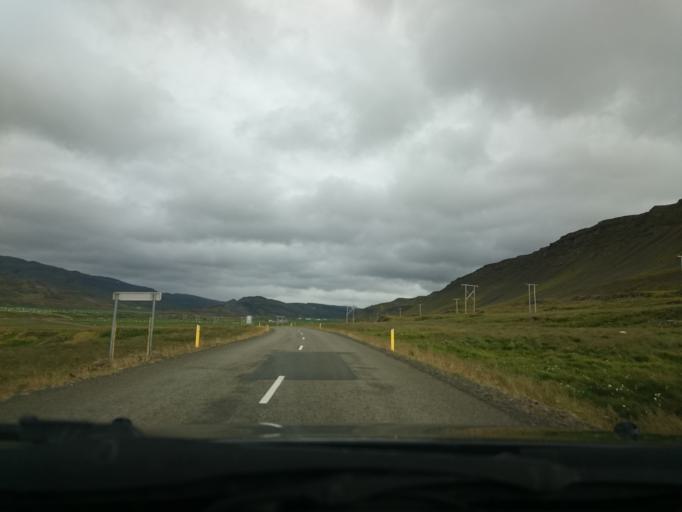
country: IS
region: West
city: Stykkisholmur
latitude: 65.4600
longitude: -21.9149
